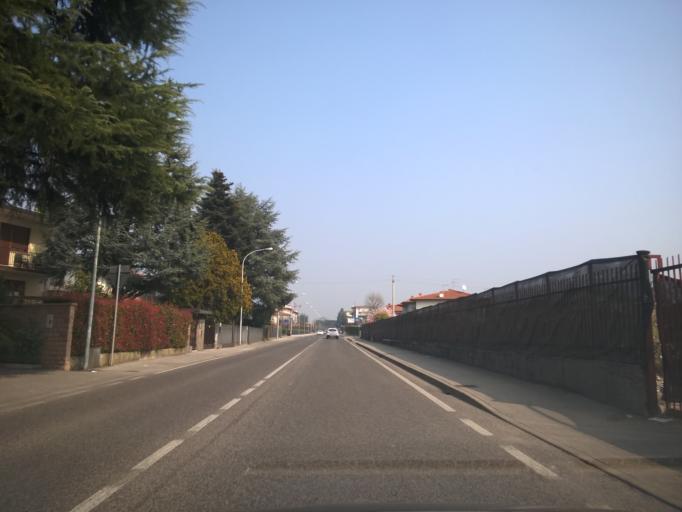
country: IT
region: Veneto
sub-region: Provincia di Vicenza
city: Thiene
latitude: 45.6978
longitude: 11.4842
